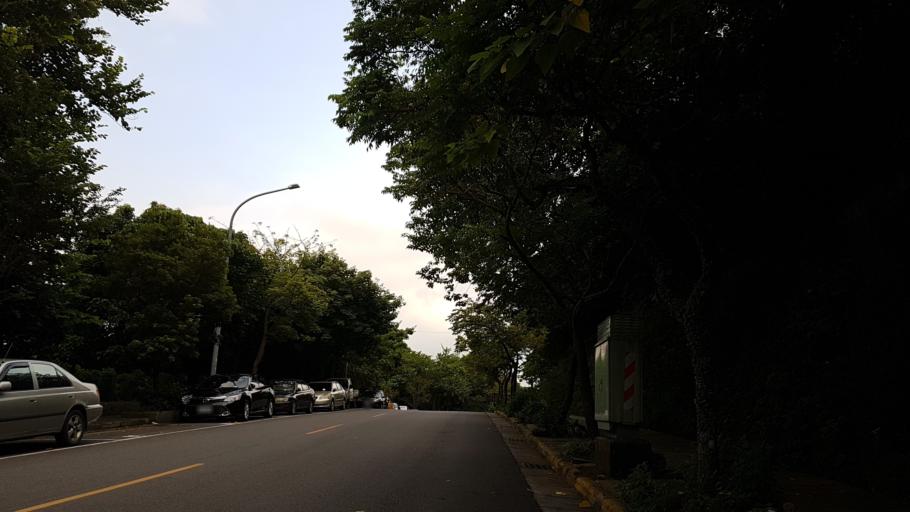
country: TW
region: Taipei
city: Taipei
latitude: 25.0046
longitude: 121.5684
